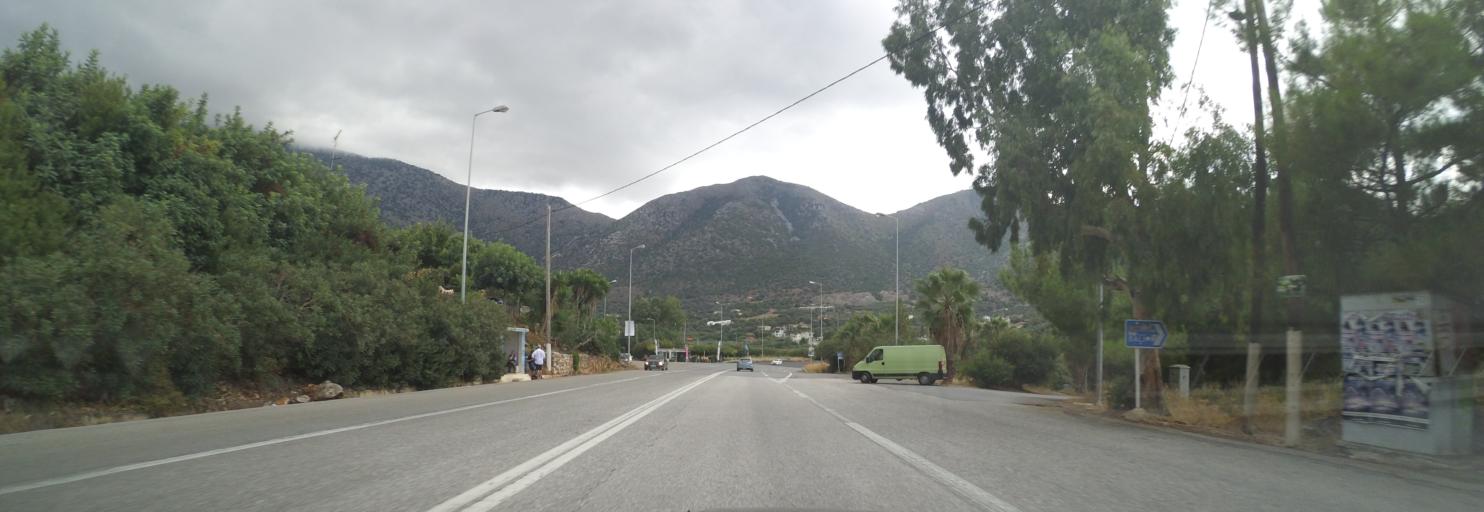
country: GR
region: Crete
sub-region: Nomos Rethymnis
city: Perama
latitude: 35.4029
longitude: 24.7871
